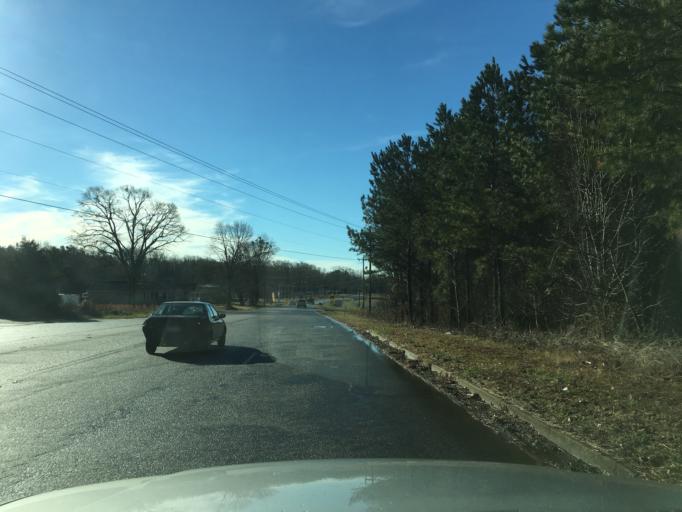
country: US
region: South Carolina
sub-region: Spartanburg County
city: Cowpens
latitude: 35.0160
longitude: -81.8727
